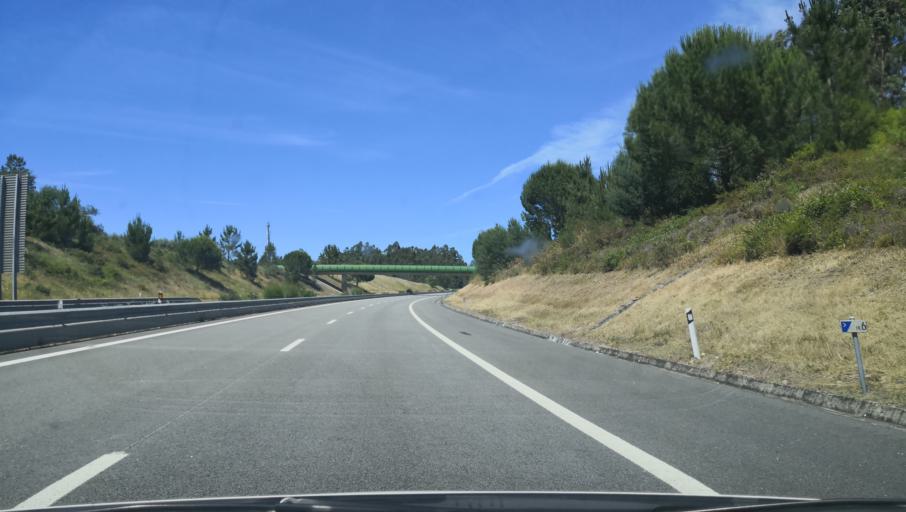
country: PT
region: Coimbra
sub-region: Montemor-O-Velho
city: Montemor-o-Velho
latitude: 40.2208
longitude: -8.6748
